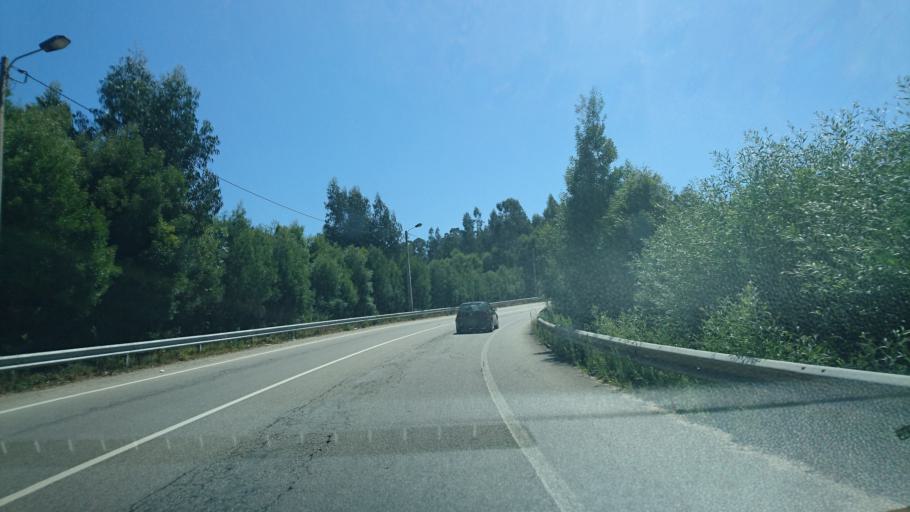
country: PT
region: Aveiro
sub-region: Ovar
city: Esmoriz
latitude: 40.9679
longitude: -8.6104
